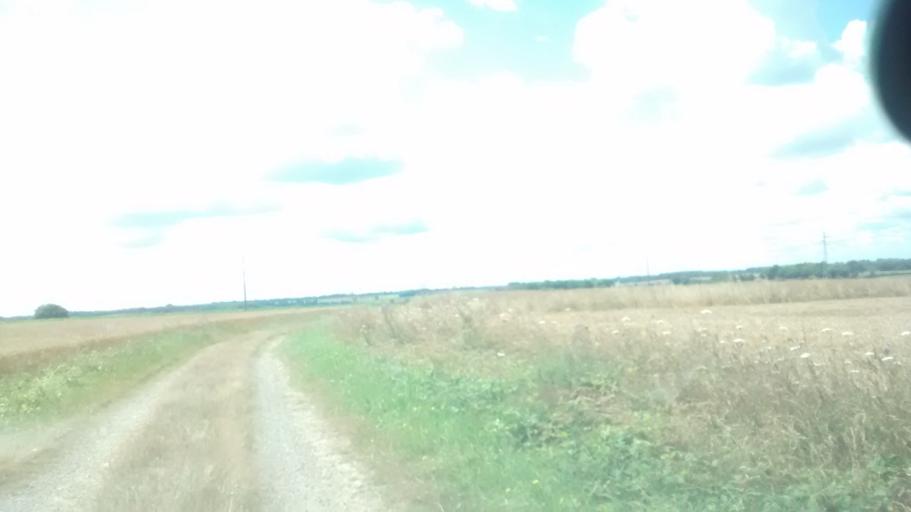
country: FR
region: Brittany
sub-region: Departement d'Ille-et-Vilaine
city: Grand-Fougeray
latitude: 47.7708
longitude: -1.7535
